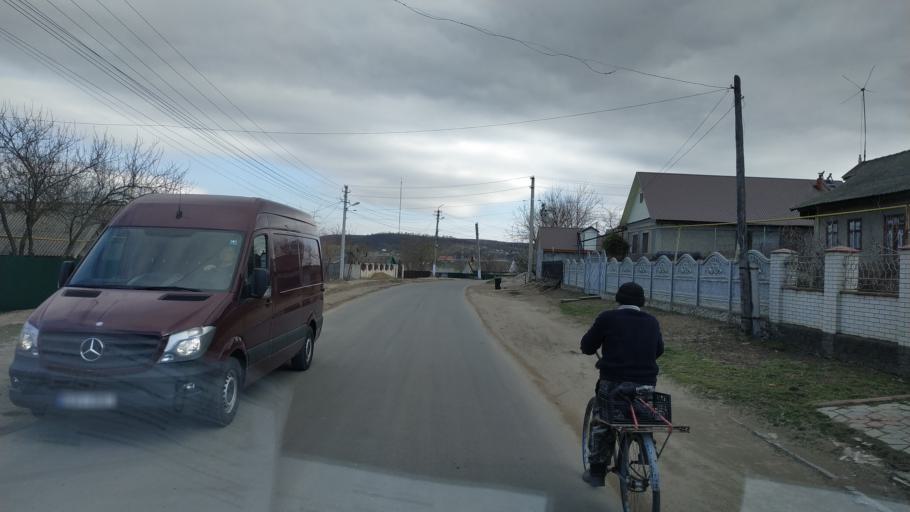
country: MD
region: Causeni
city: Causeni
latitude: 46.6440
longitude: 29.3935
